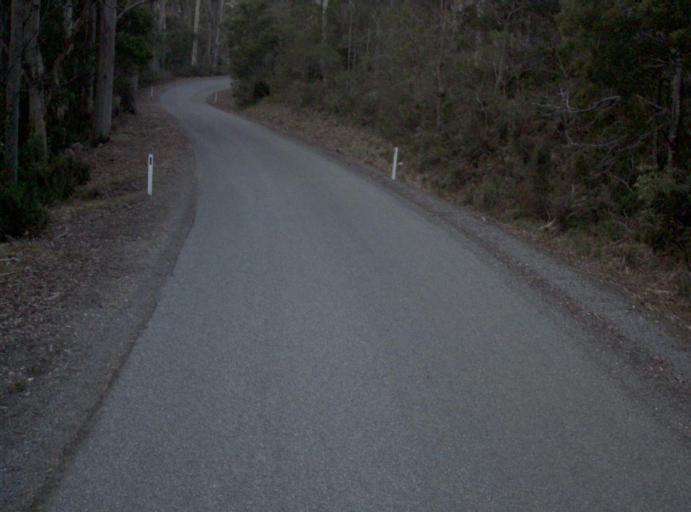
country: AU
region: Tasmania
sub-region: Launceston
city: Newstead
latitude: -41.3118
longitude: 147.3333
